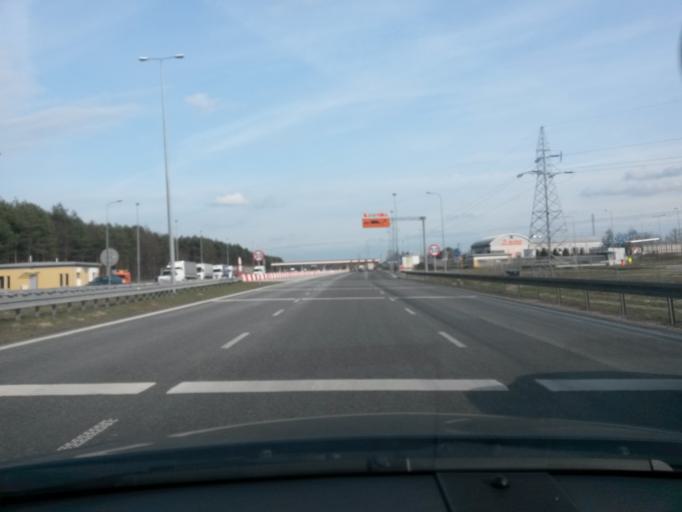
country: PL
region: Greater Poland Voivodeship
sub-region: Powiat koninski
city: Stare Miasto
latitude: 52.1539
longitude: 18.2730
